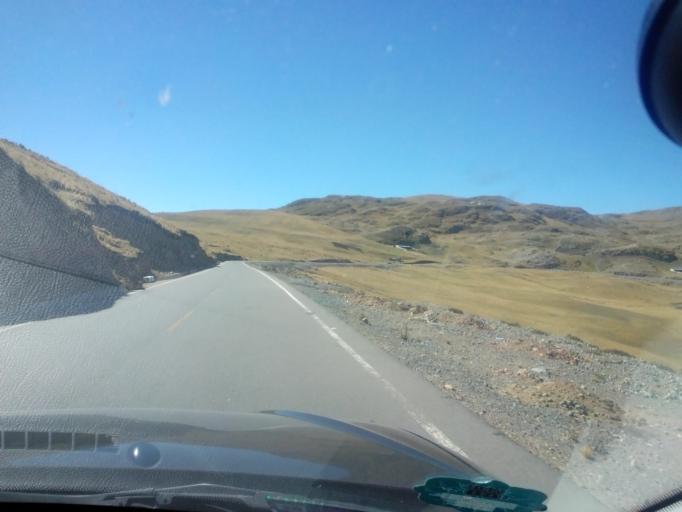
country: PE
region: Apurimac
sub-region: Chincheros
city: Ranracancha
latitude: -13.6067
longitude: -73.5795
